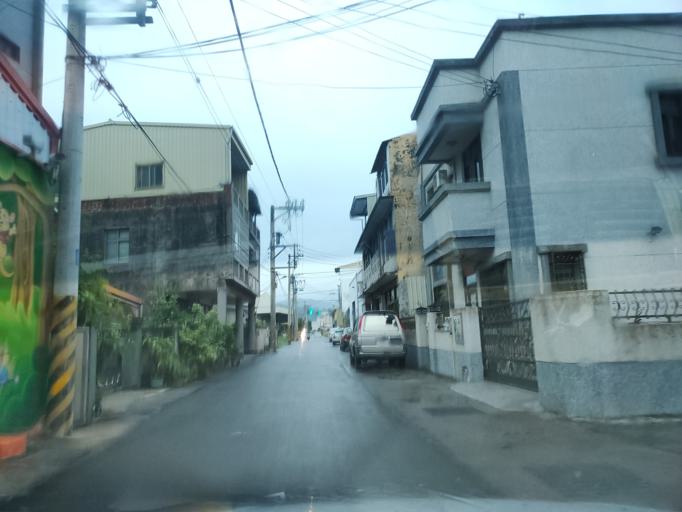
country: TW
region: Taiwan
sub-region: Miaoli
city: Miaoli
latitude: 24.5594
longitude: 120.8267
